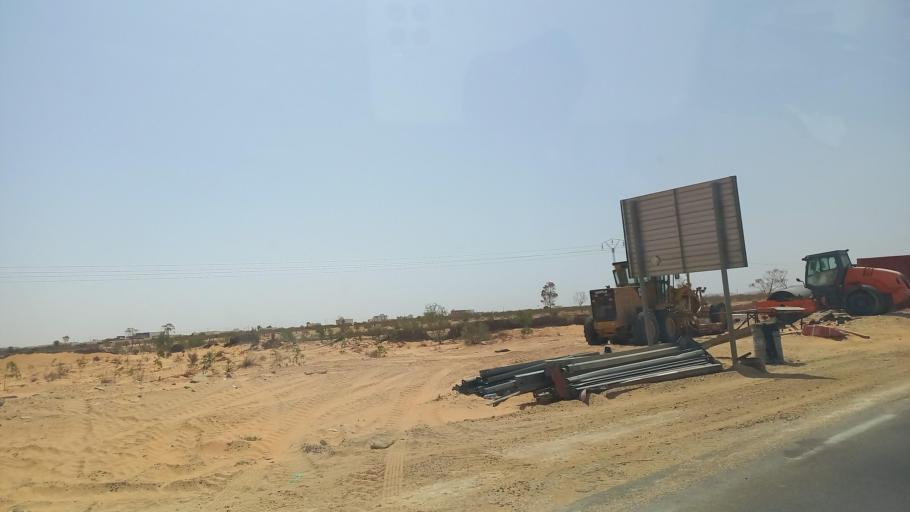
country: TN
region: Madanin
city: Medenine
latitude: 33.2084
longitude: 10.4456
